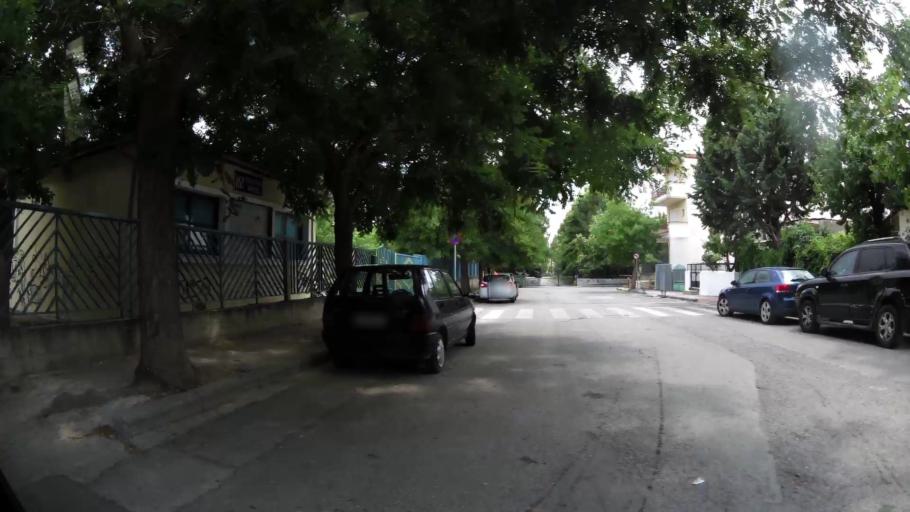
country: GR
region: West Macedonia
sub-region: Nomos Kozanis
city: Kozani
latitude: 40.2974
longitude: 21.7992
